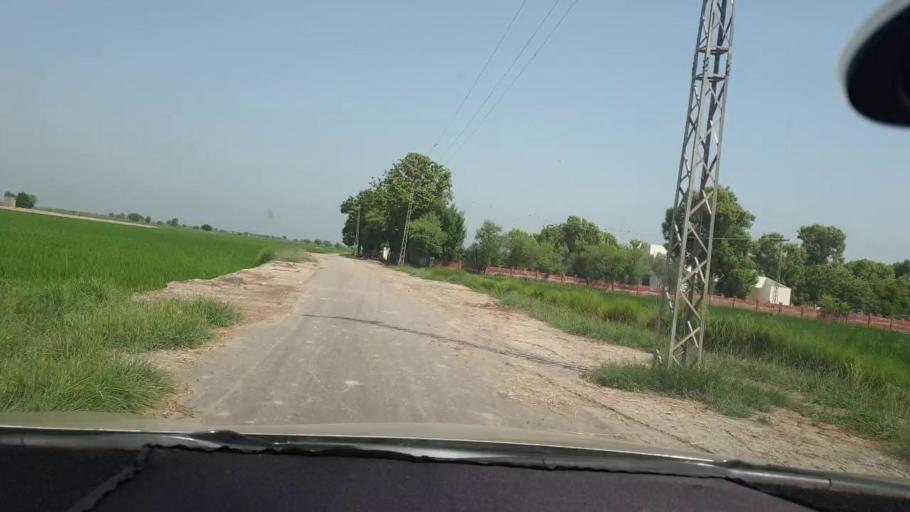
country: PK
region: Sindh
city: Goth Garelo
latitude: 27.4981
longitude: 68.0212
